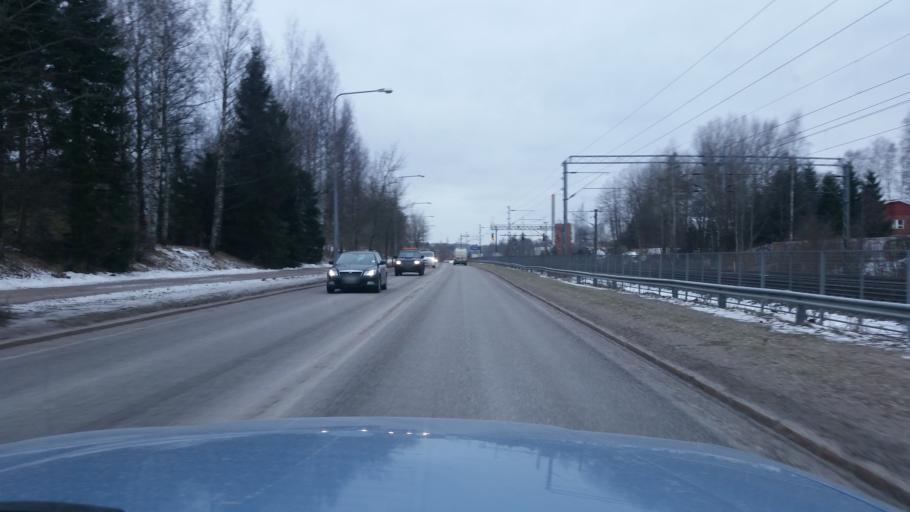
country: FI
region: Uusimaa
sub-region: Helsinki
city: Vantaa
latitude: 60.2453
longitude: 25.0000
